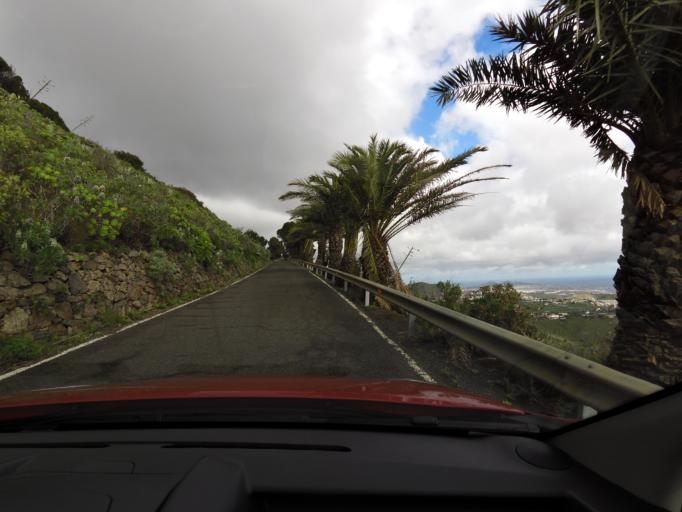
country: ES
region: Canary Islands
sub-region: Provincia de Las Palmas
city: Santa Brigida
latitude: 28.0372
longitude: -15.4559
